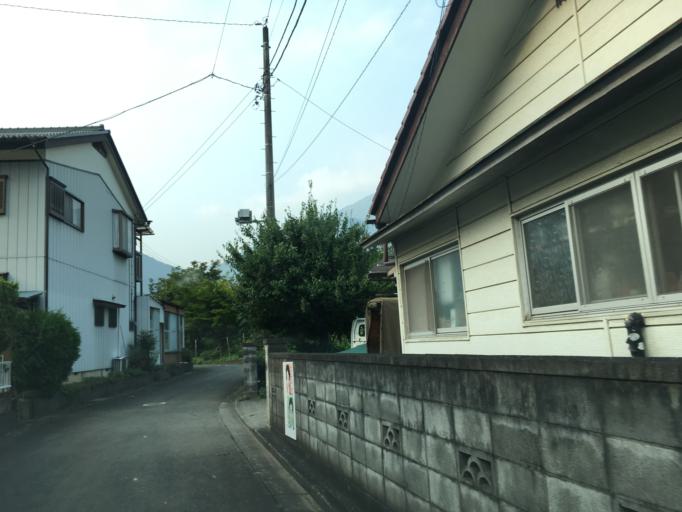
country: JP
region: Saitama
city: Chichibu
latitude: 35.9844
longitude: 139.1123
